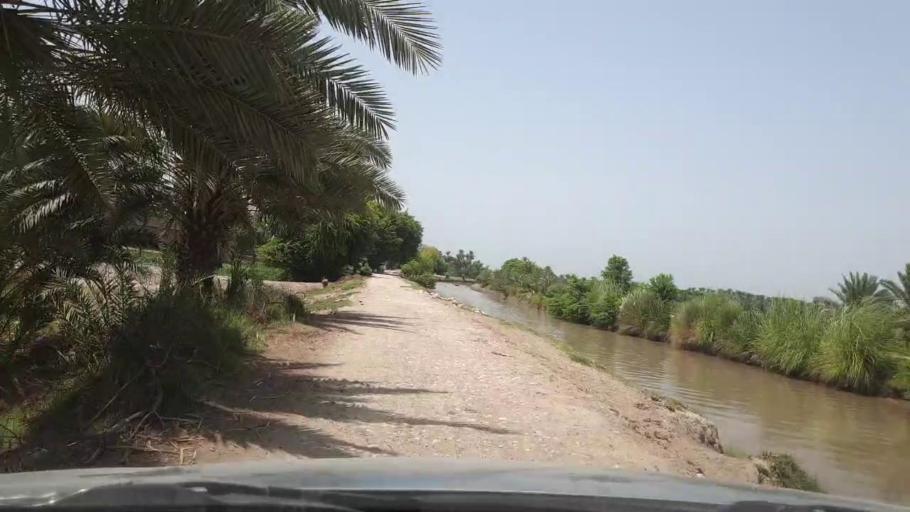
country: PK
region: Sindh
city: Pano Aqil
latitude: 27.8928
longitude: 69.1382
